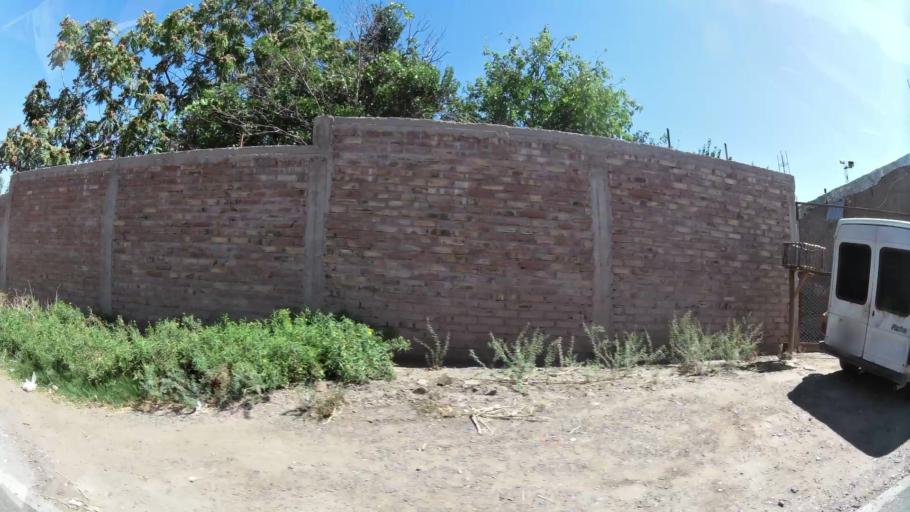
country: AR
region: Mendoza
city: Villa Nueva
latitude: -32.8705
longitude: -68.7854
